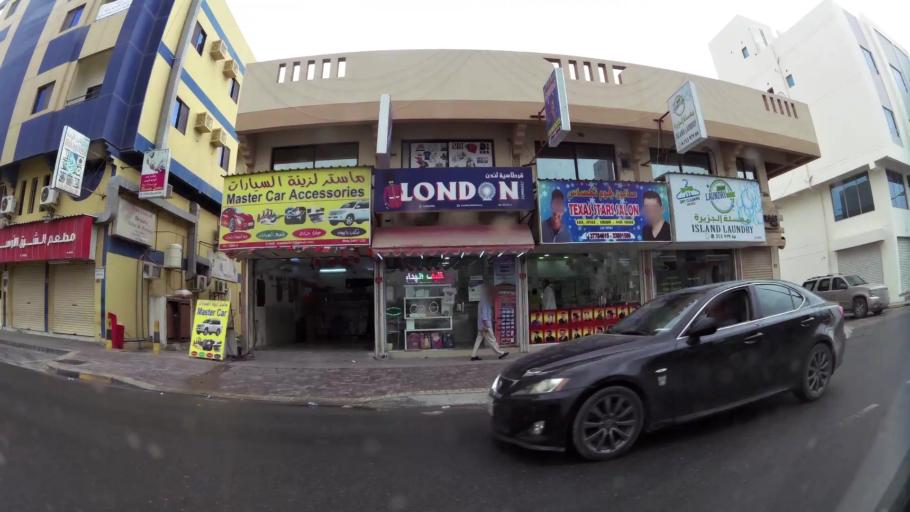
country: BH
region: Northern
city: Ar Rifa'
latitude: 26.1283
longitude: 50.5663
